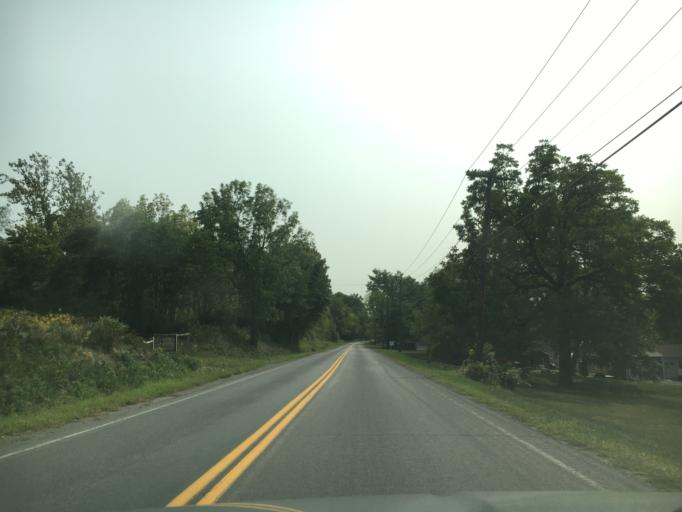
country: US
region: New York
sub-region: Steuben County
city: Sylvan Beach
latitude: 42.4559
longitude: -77.0983
